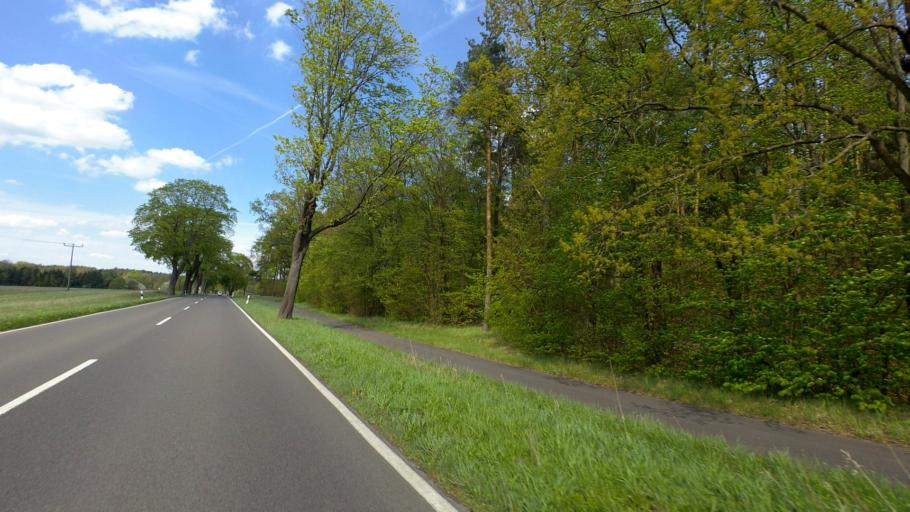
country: DE
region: Brandenburg
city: Milmersdorf
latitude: 53.0691
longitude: 13.6233
